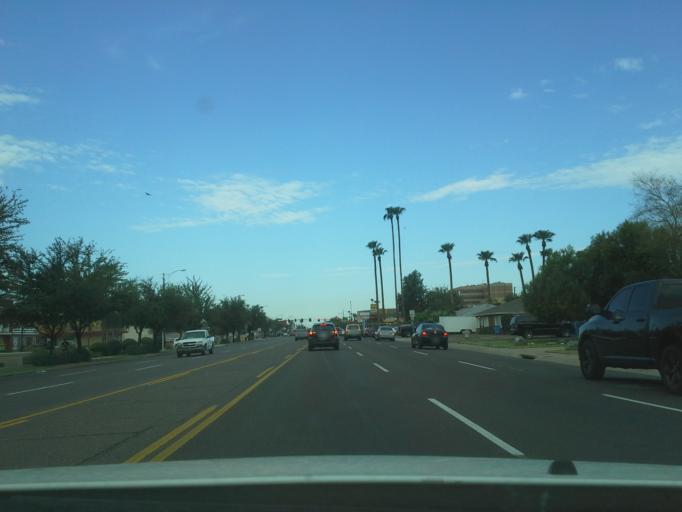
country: US
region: Arizona
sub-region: Maricopa County
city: Phoenix
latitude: 33.5241
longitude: -112.0964
